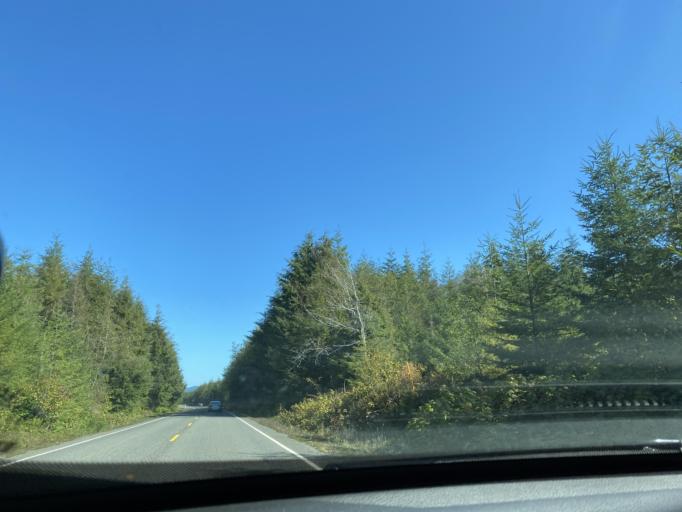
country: US
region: Washington
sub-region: Clallam County
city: Forks
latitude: 47.9271
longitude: -124.4900
